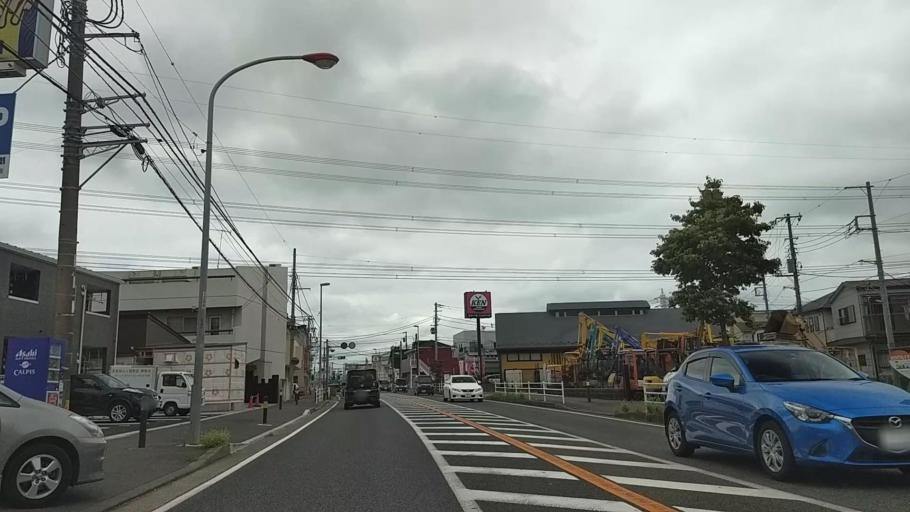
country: JP
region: Kanagawa
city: Minami-rinkan
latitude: 35.4216
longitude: 139.4690
